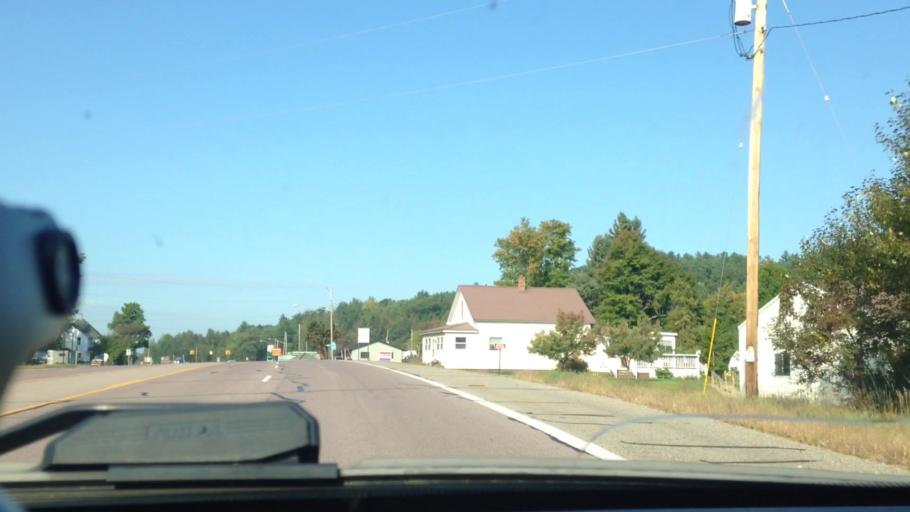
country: US
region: Michigan
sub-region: Dickinson County
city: Quinnesec
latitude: 45.8066
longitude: -87.9843
